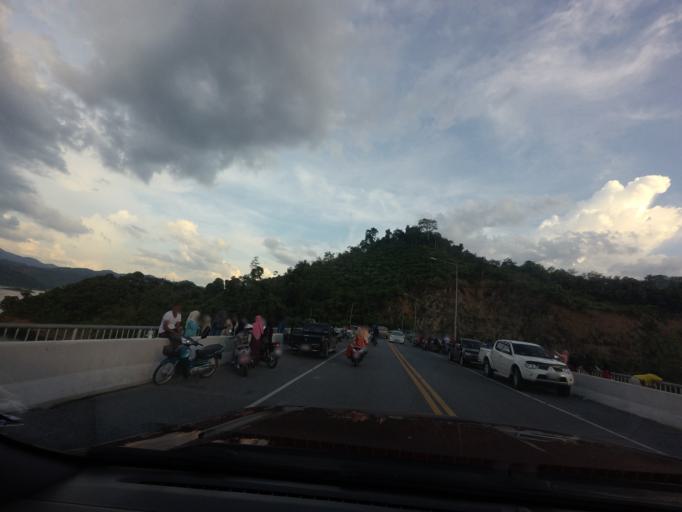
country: TH
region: Yala
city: Than To
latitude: 6.0482
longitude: 101.1974
